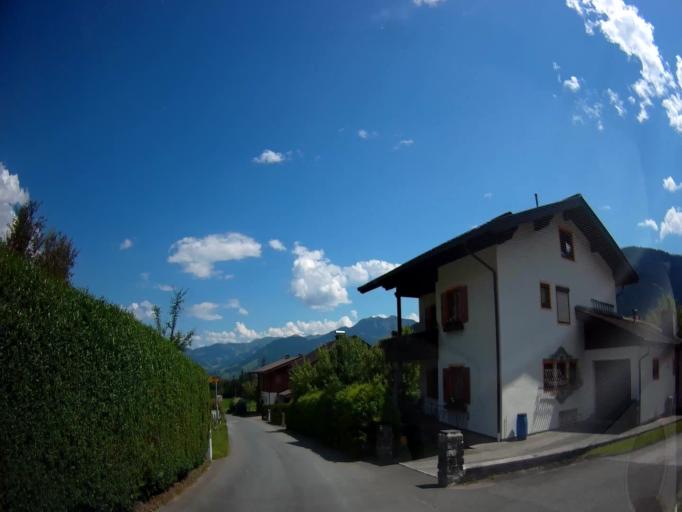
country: AT
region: Salzburg
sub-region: Politischer Bezirk Zell am See
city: Leogang
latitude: 47.4508
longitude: 12.7960
